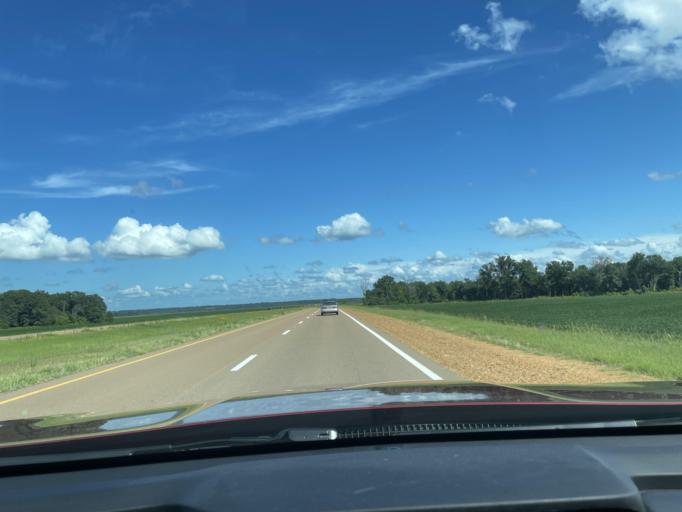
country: US
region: Mississippi
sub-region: Yazoo County
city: Yazoo City
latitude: 32.9584
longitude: -90.4314
